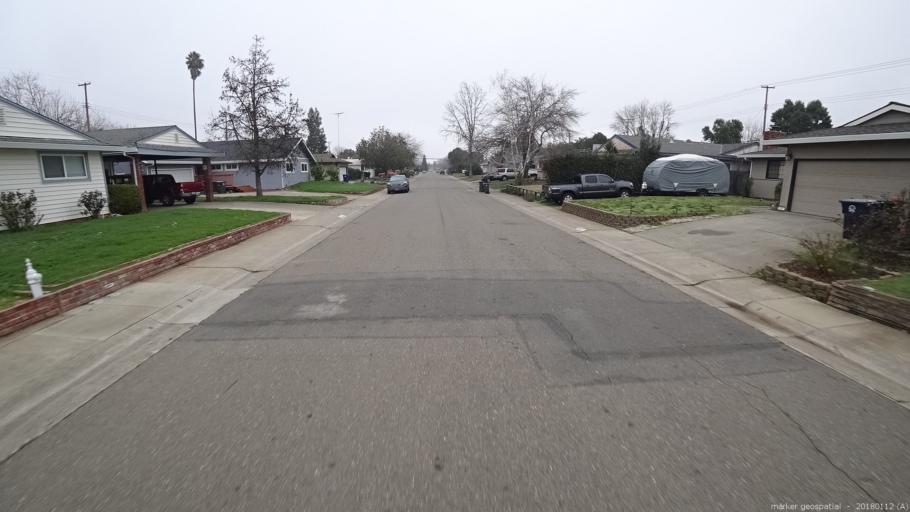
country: US
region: California
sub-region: Sacramento County
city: Rancho Cordova
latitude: 38.6017
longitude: -121.2819
